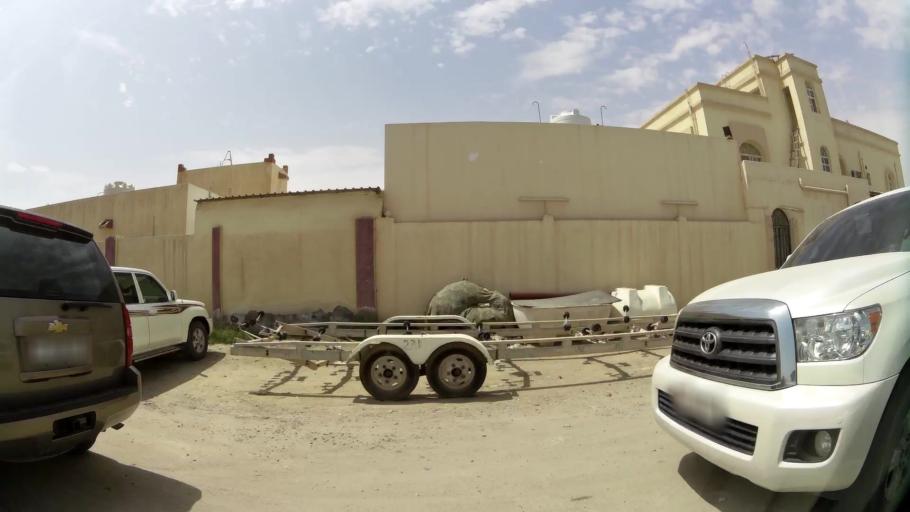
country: QA
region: Baladiyat ar Rayyan
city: Ar Rayyan
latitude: 25.3539
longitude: 51.4763
